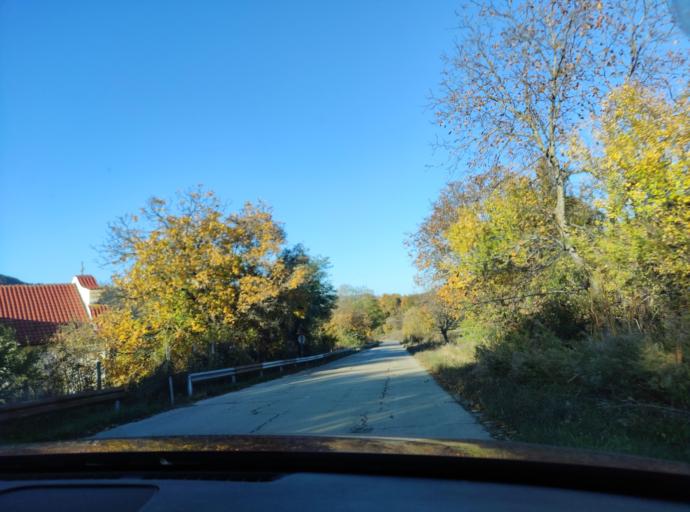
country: BG
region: Montana
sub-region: Obshtina Chiprovtsi
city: Chiprovtsi
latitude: 43.3849
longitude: 22.9205
